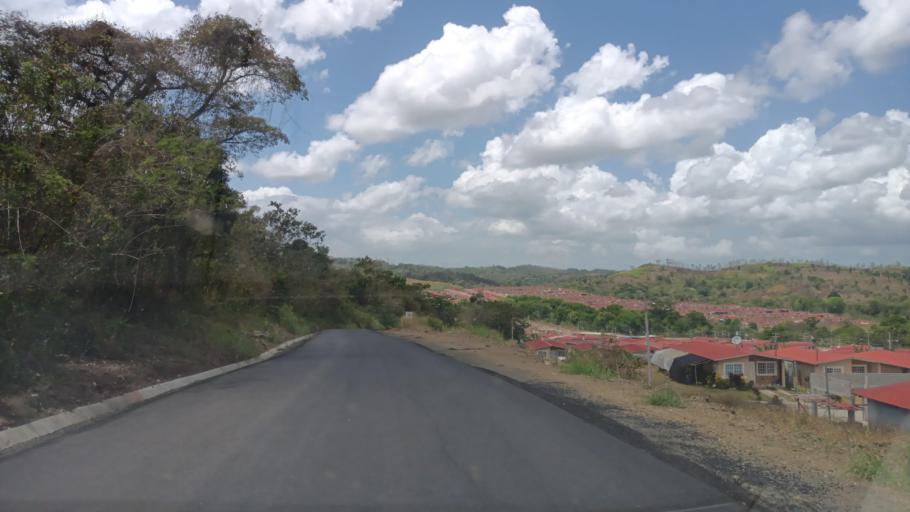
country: PA
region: Panama
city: Alcalde Diaz
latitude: 9.0984
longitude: -79.5694
